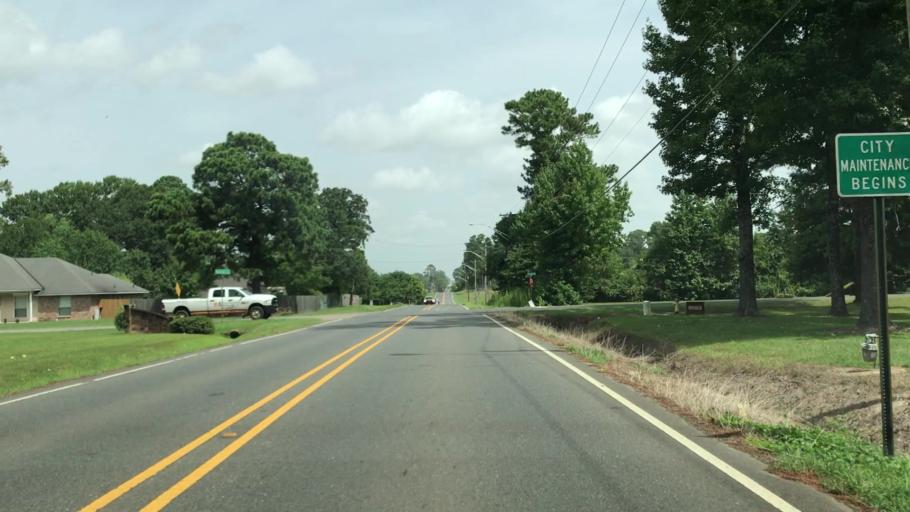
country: US
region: Louisiana
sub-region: De Soto Parish
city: Stonewall
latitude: 32.3846
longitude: -93.7634
